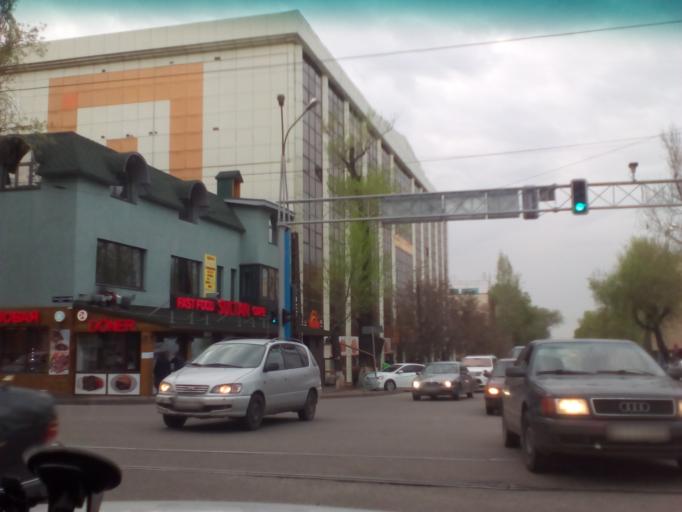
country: KZ
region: Almaty Qalasy
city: Almaty
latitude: 43.2641
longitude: 76.9491
